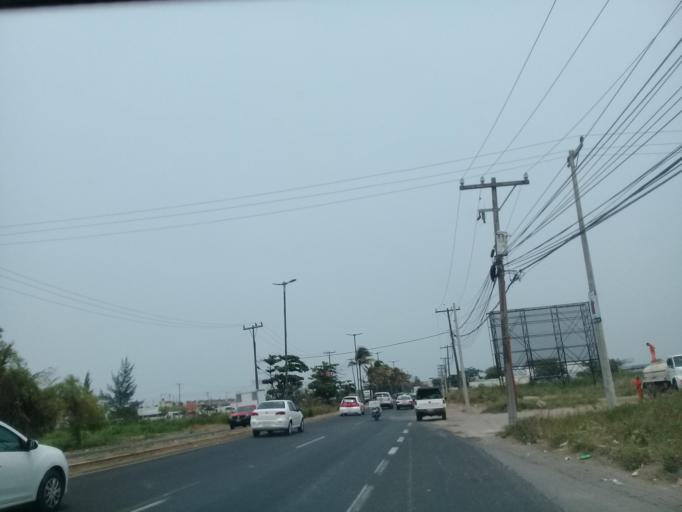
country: MX
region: Veracruz
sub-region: Veracruz
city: Hacienda Sotavento
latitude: 19.1487
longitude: -96.1714
